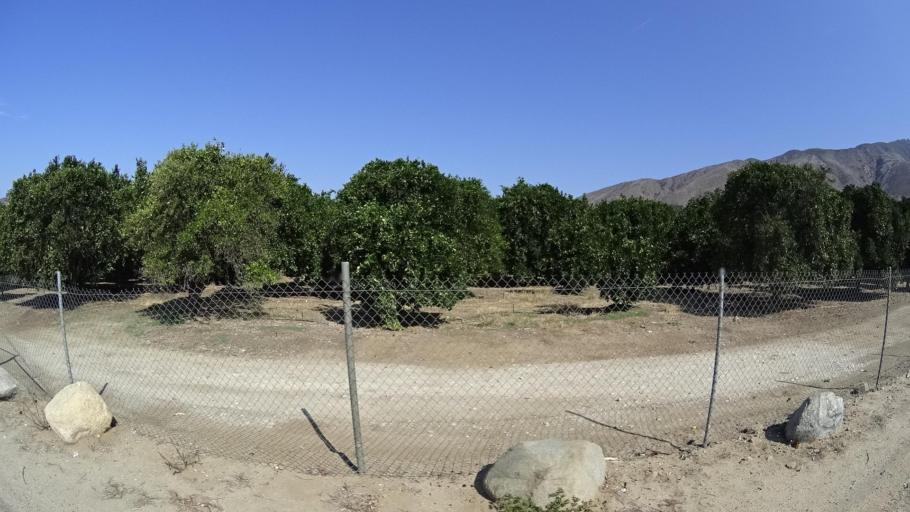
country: US
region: California
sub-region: San Diego County
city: Valley Center
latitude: 33.3326
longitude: -116.9953
